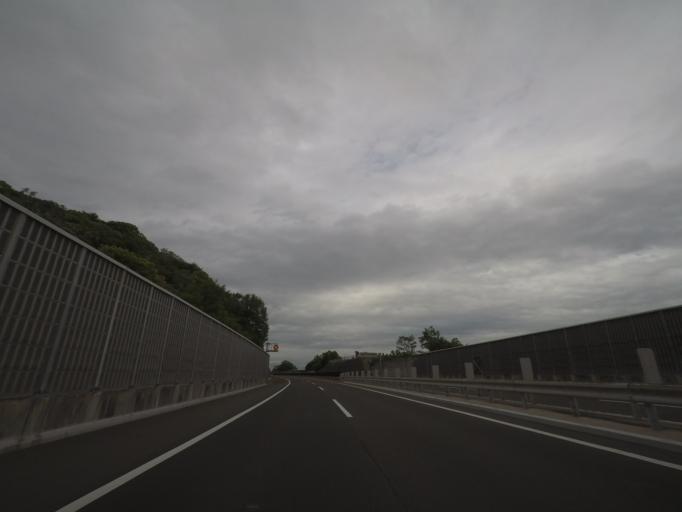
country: JP
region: Kagawa
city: Sakaidecho
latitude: 34.3147
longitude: 133.8389
